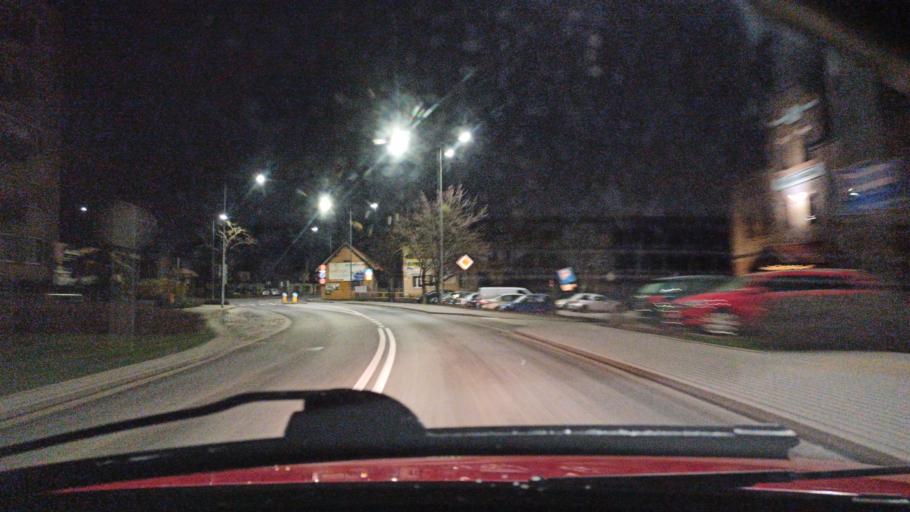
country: PL
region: Warmian-Masurian Voivodeship
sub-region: Powiat elblaski
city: Elblag
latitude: 54.1675
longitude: 19.4156
